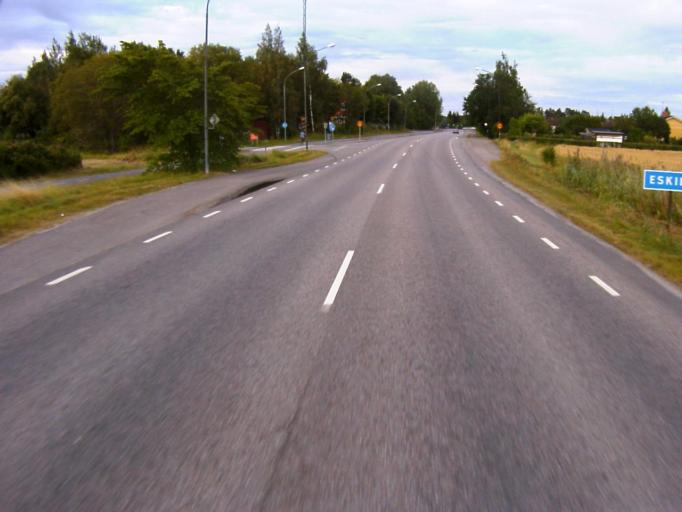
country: SE
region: Soedermanland
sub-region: Eskilstuna Kommun
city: Torshalla
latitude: 59.4022
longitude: 16.4855
